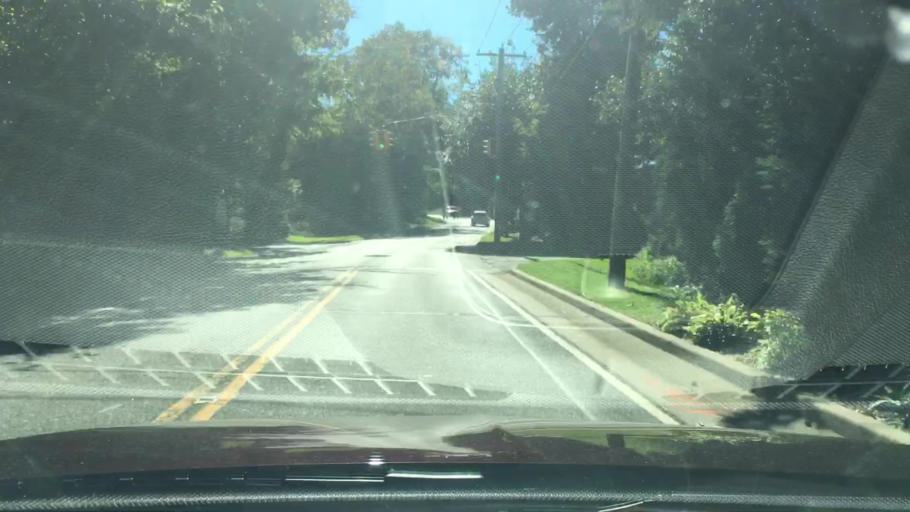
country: US
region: New York
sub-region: Nassau County
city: Plandome
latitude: 40.8079
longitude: -73.7069
